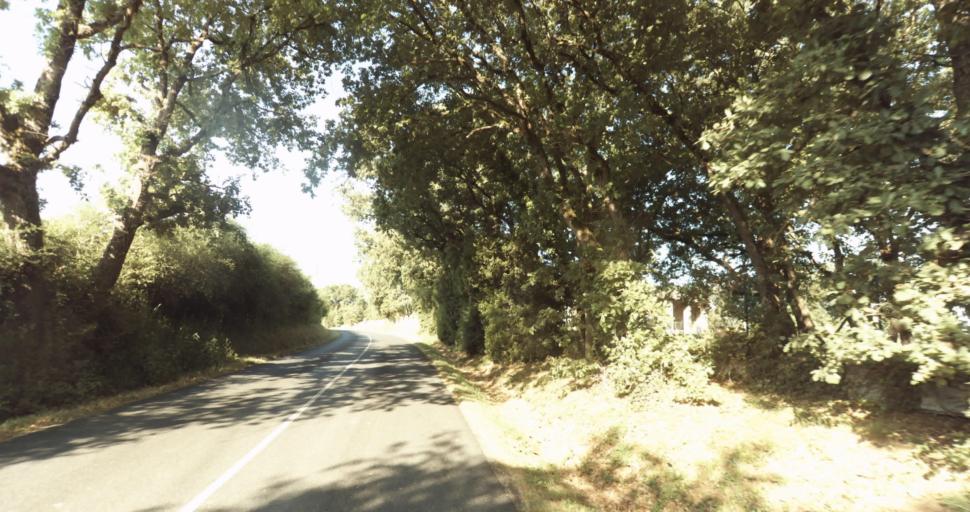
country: FR
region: Midi-Pyrenees
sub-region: Departement de la Haute-Garonne
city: Fontenilles
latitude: 43.5610
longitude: 1.2034
